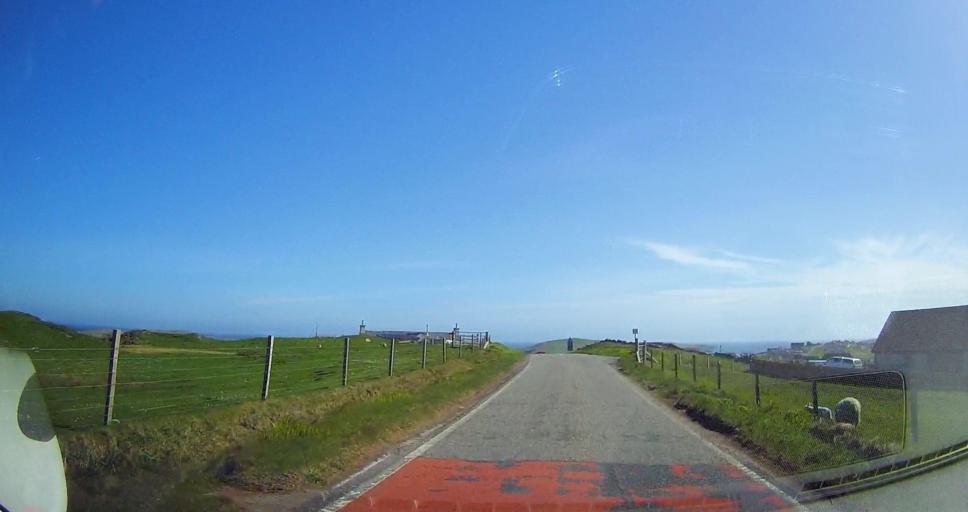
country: GB
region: Scotland
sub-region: Shetland Islands
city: Sandwick
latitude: 60.0146
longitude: -1.2279
